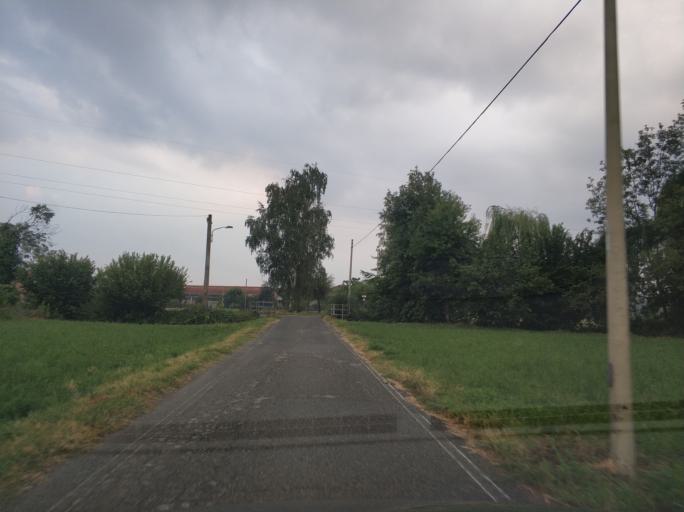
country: IT
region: Piedmont
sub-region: Provincia di Torino
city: Robassomero
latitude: 45.2074
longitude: 7.5846
